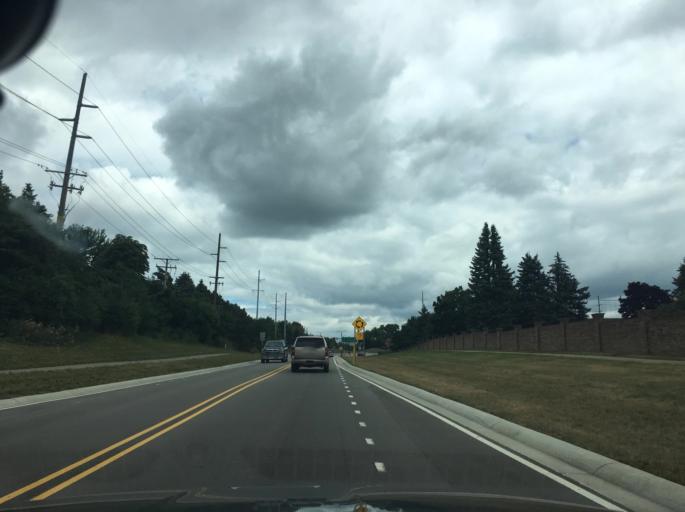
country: US
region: Michigan
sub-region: Oakland County
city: Rochester
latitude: 42.6929
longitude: -83.1538
